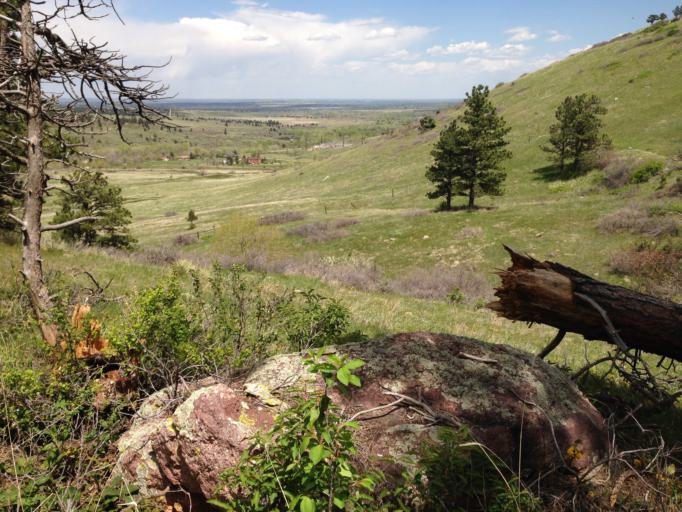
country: US
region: Colorado
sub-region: Boulder County
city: Boulder
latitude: 39.9275
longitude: -105.2704
